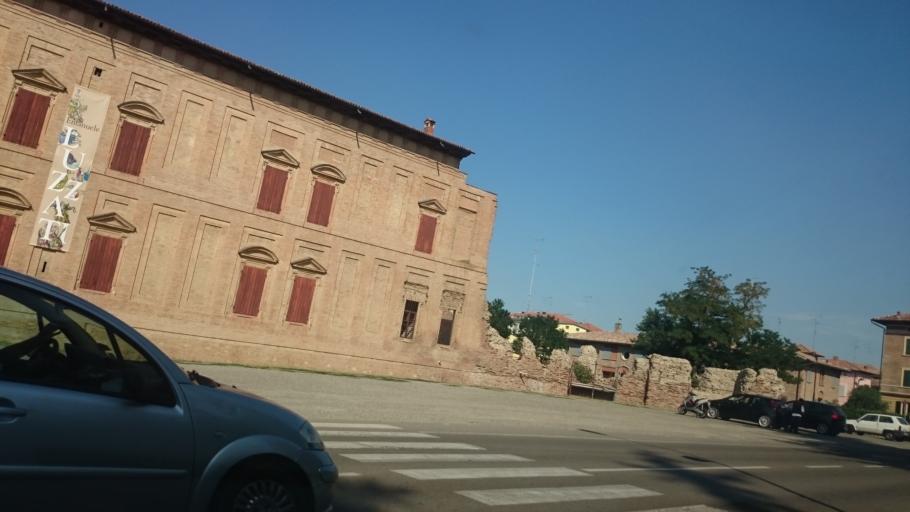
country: IT
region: Emilia-Romagna
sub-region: Provincia di Reggio Emilia
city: Scandiano
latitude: 44.5977
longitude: 10.6868
